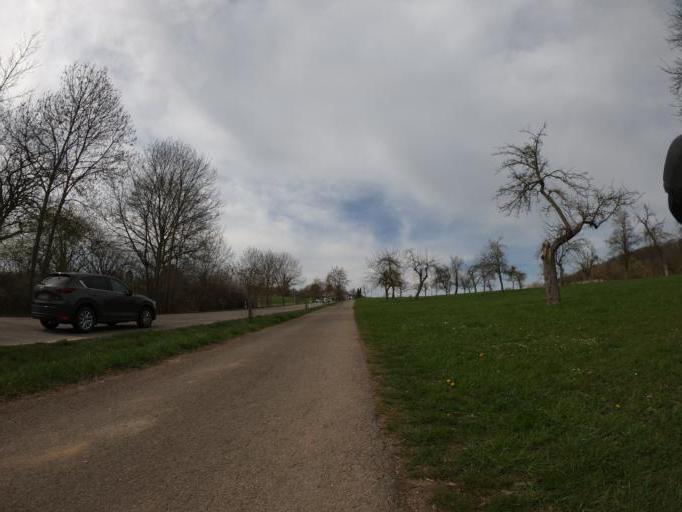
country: DE
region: Baden-Wuerttemberg
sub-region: Regierungsbezirk Stuttgart
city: Ostfildern
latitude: 48.7142
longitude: 9.2382
